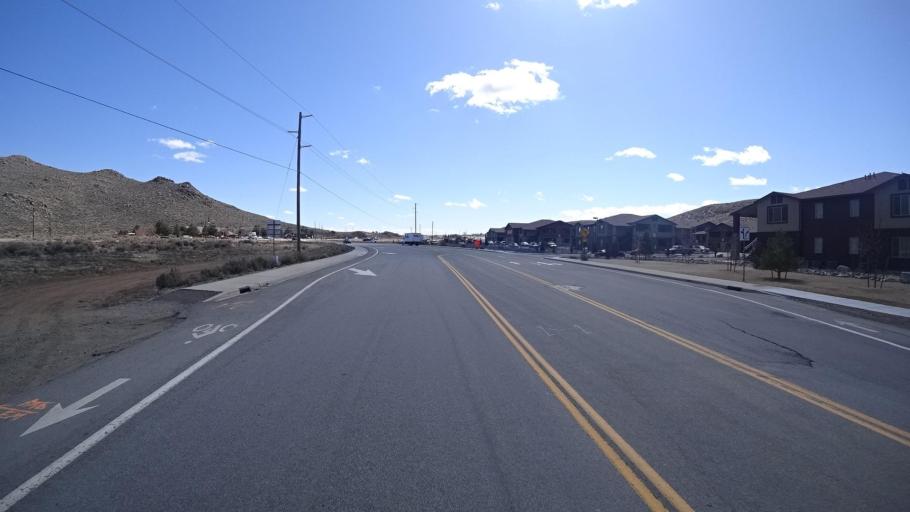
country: US
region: Nevada
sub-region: Washoe County
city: Lemmon Valley
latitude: 39.6249
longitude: -119.8500
